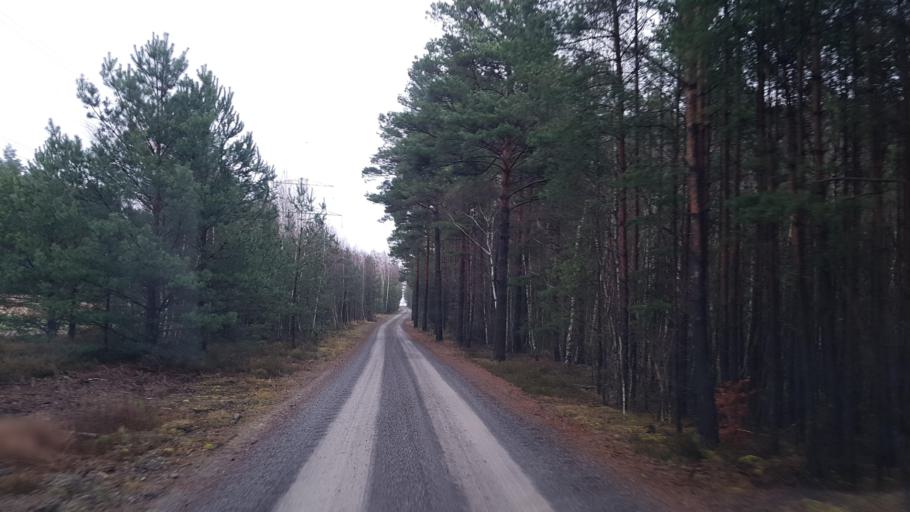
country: DE
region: Brandenburg
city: Altdobern
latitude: 51.6378
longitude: 13.9865
